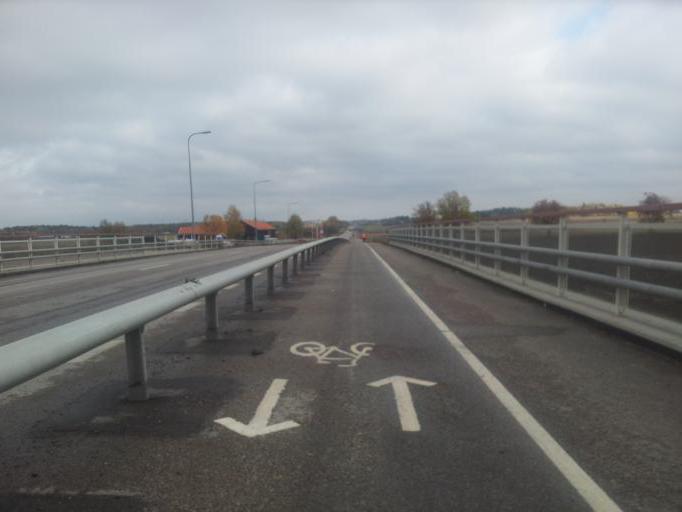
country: SE
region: Uppsala
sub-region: Uppsala Kommun
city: Uppsala
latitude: 59.8814
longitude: 17.6865
